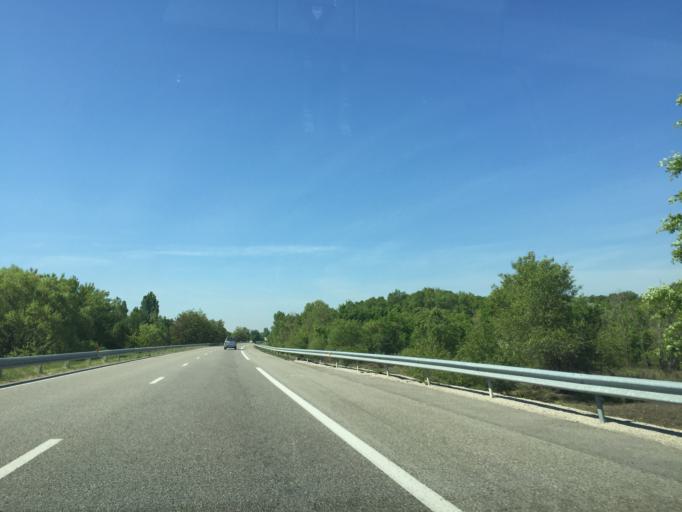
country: FR
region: Provence-Alpes-Cote d'Azur
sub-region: Departement des Alpes-de-Haute-Provence
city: Volx
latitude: 43.8272
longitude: 5.8391
